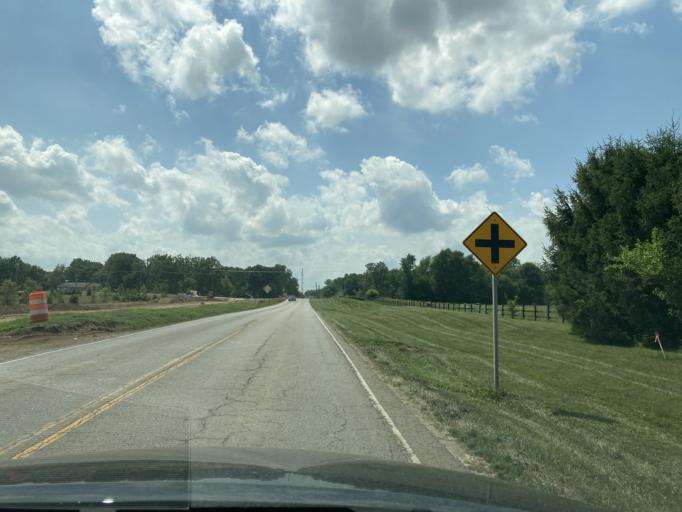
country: US
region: Indiana
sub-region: Boone County
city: Zionsville
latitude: 39.9988
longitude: -86.2361
